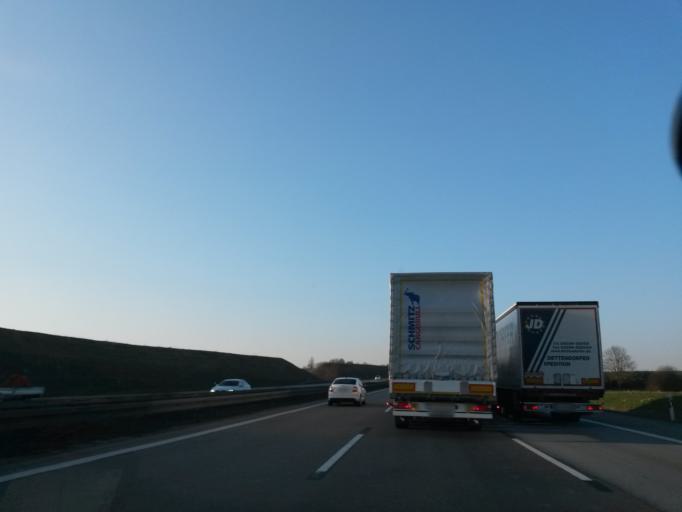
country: DE
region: Bavaria
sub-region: Upper Bavaria
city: Stammham
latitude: 48.8482
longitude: 11.4655
